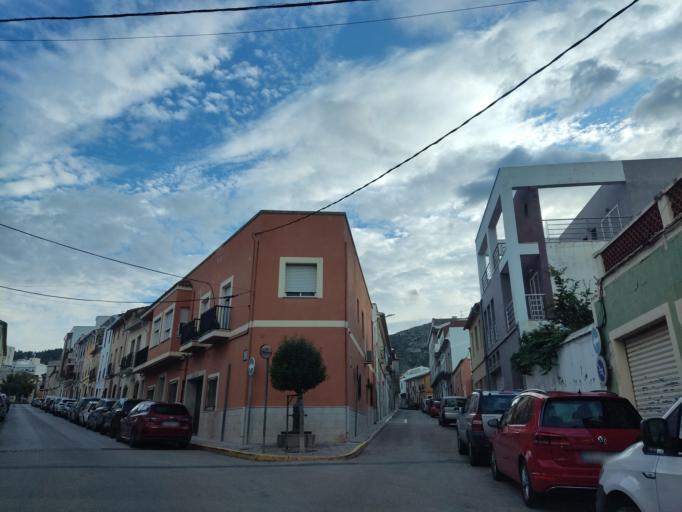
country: ES
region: Valencia
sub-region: Provincia de Alicante
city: Pedreguer
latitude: 38.7963
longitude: 0.0324
